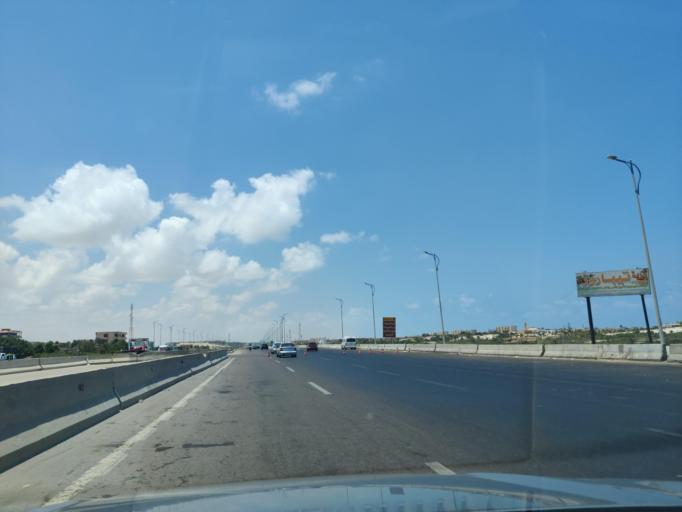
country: EG
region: Muhafazat Matruh
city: Al `Alamayn
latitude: 30.8975
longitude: 29.4078
